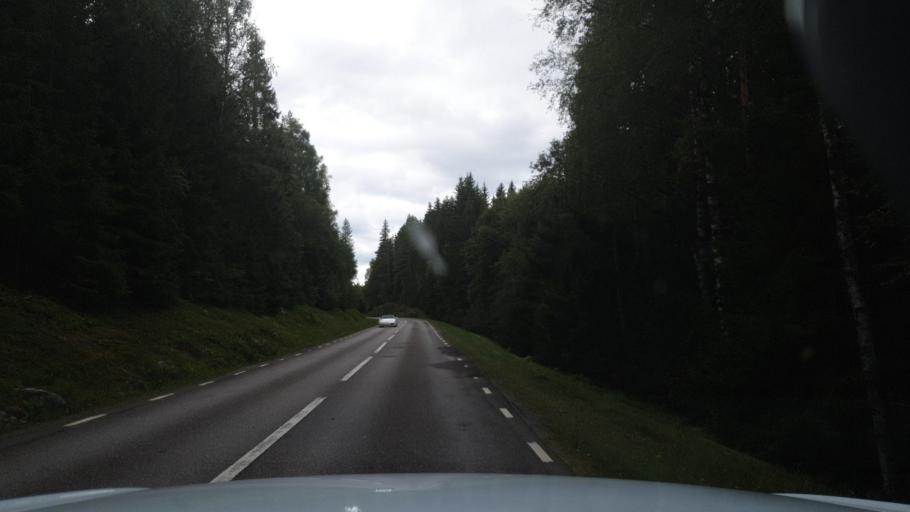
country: SE
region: Vaermland
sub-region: Eda Kommun
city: Amotfors
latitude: 59.6574
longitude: 12.3749
